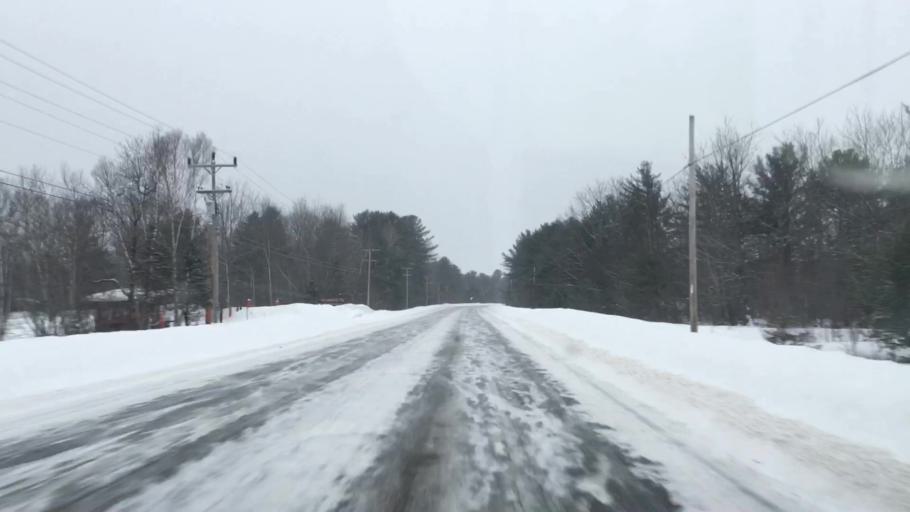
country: US
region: Maine
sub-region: Penobscot County
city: Medway
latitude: 45.5629
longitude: -68.3954
